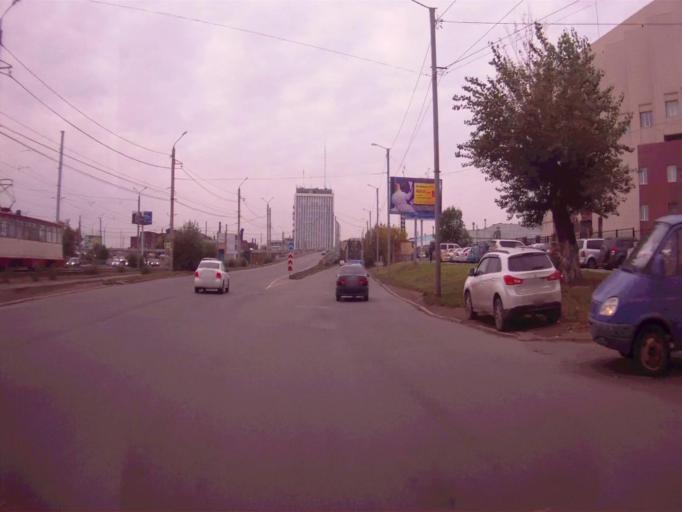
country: RU
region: Chelyabinsk
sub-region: Gorod Chelyabinsk
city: Chelyabinsk
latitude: 55.1401
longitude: 61.4117
